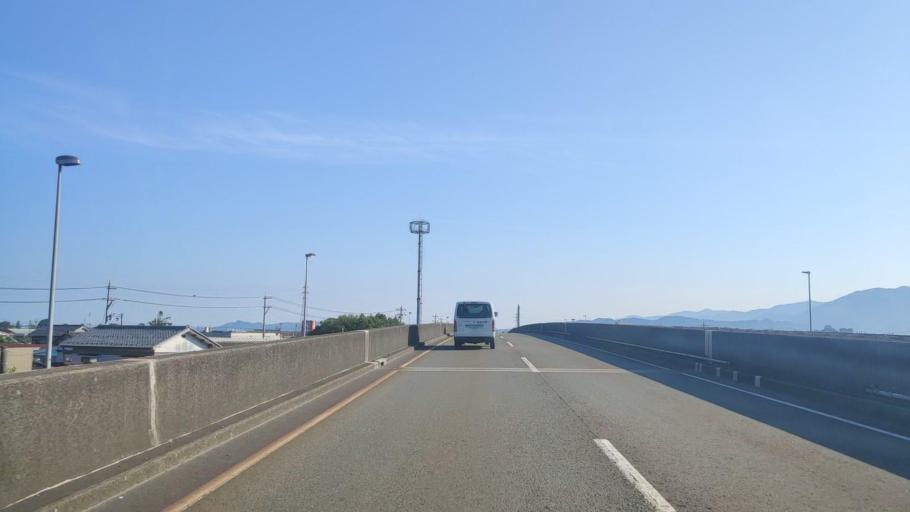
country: JP
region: Fukui
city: Maruoka
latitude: 36.1423
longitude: 136.2639
